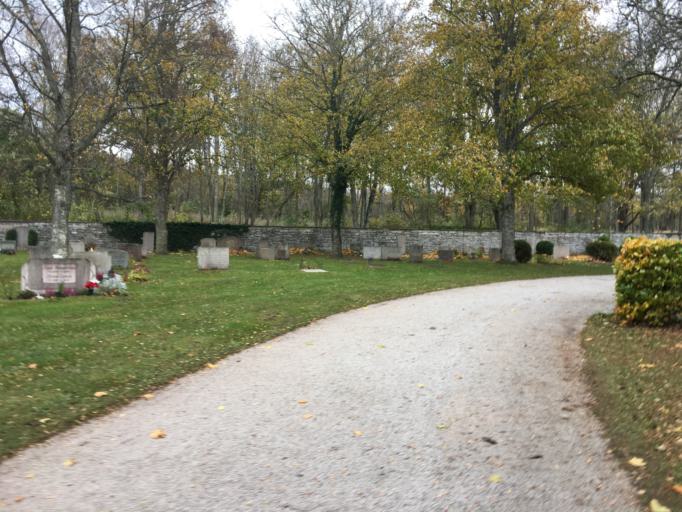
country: SE
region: Gotland
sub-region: Gotland
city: Visby
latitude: 57.6586
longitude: 18.3173
